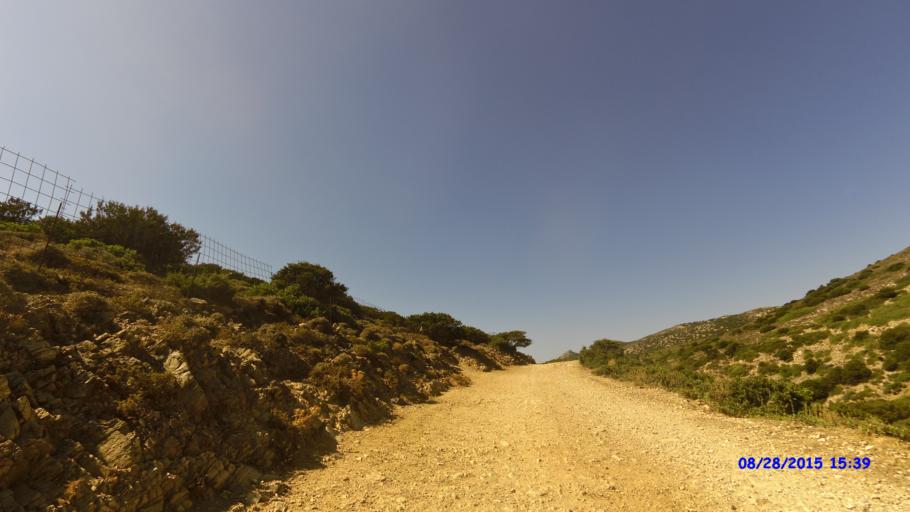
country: GR
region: South Aegean
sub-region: Nomos Kykladon
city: Antiparos
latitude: 36.9872
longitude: 25.0293
